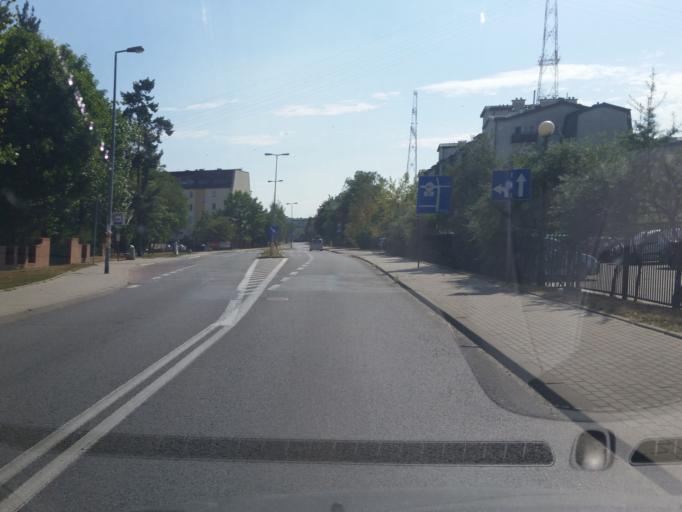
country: PL
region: Masovian Voivodeship
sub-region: Warszawa
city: Bielany
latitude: 52.3287
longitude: 20.9363
